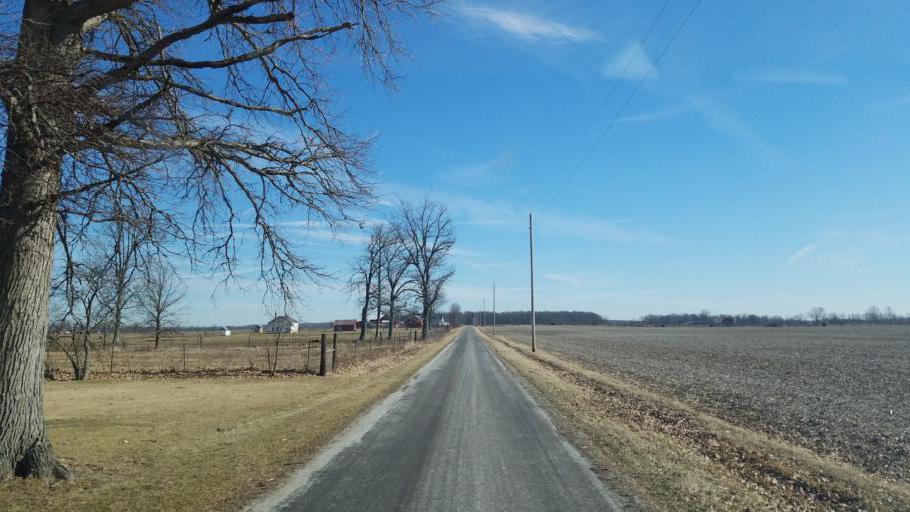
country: US
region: Ohio
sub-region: Hardin County
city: Kenton
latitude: 40.5995
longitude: -83.4797
